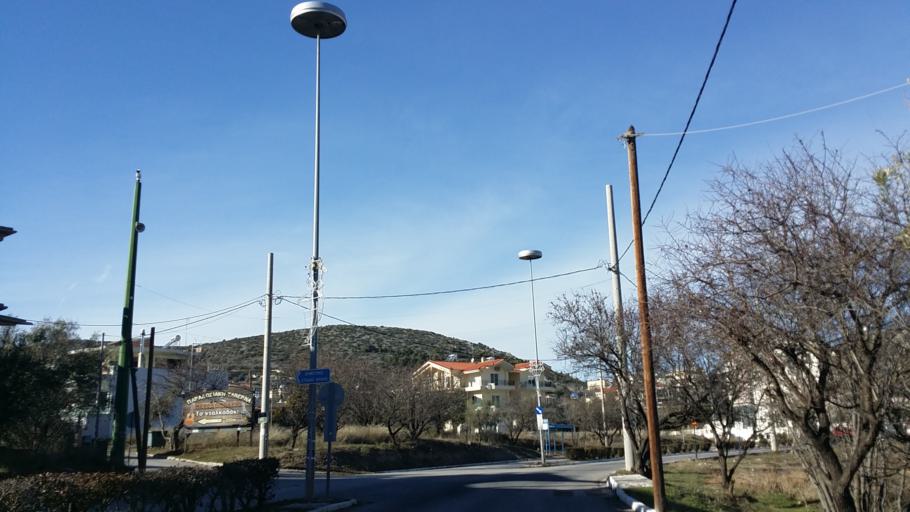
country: GR
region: Attica
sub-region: Nomarchia Dytikis Attikis
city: Fyli
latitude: 38.0989
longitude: 23.6689
